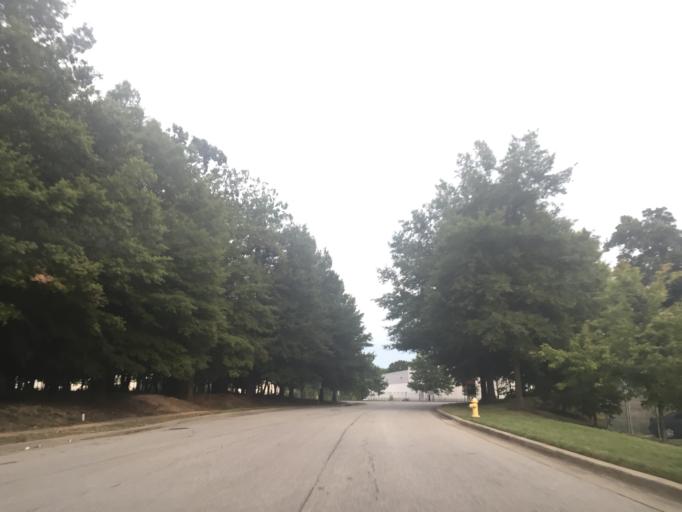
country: US
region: Maryland
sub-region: Anne Arundel County
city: Riviera Beach
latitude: 39.1961
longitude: -76.5517
